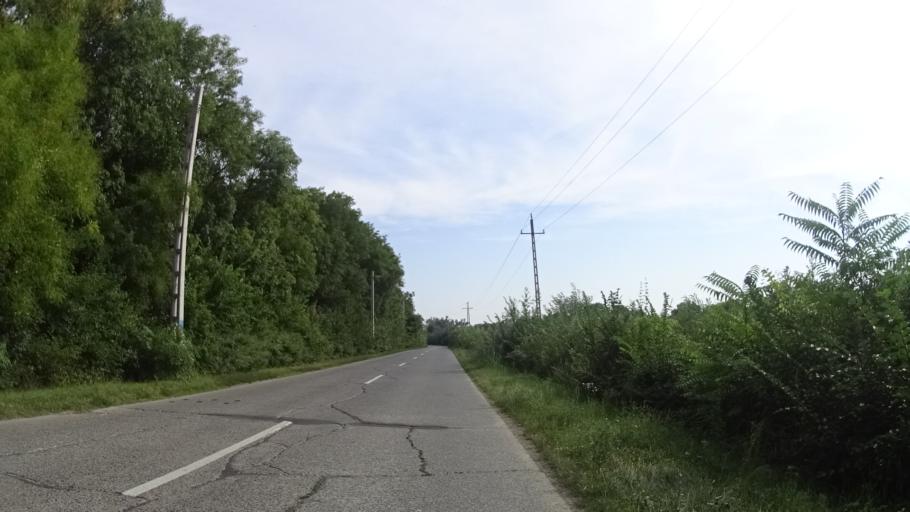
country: HU
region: Fejer
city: Polgardi
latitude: 47.0702
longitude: 18.3108
